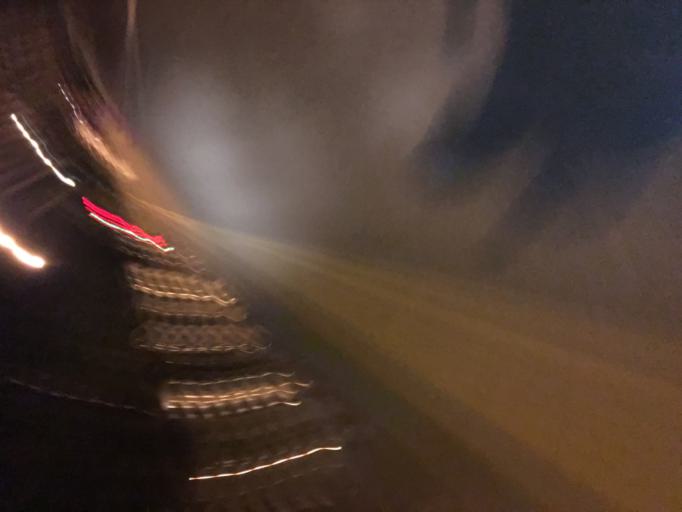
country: TW
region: Taiwan
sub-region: Hsinchu
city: Zhubei
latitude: 24.8427
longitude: 120.9985
